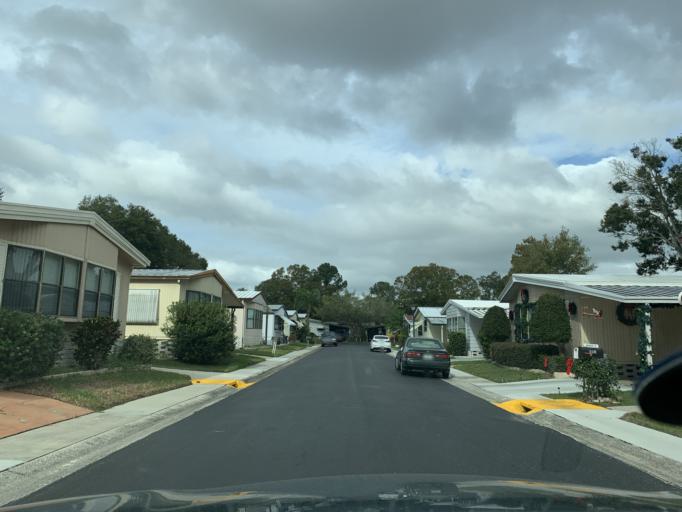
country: US
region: Florida
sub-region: Pinellas County
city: Ridgecrest
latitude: 27.8809
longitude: -82.7946
